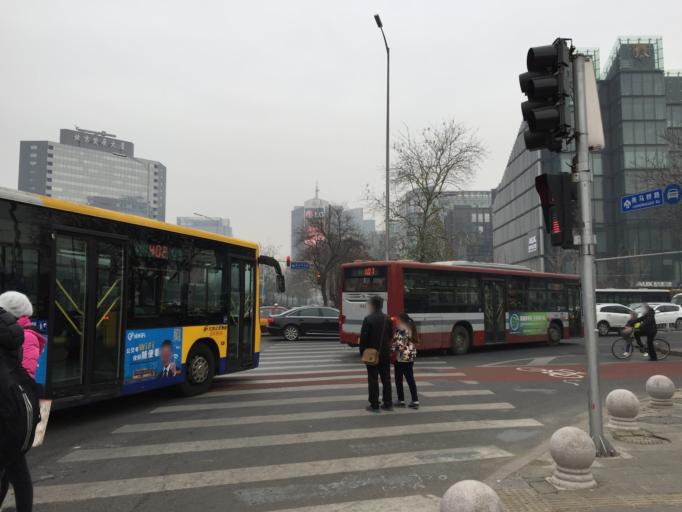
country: CN
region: Beijing
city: Chaowai
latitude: 39.9478
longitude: 116.4560
